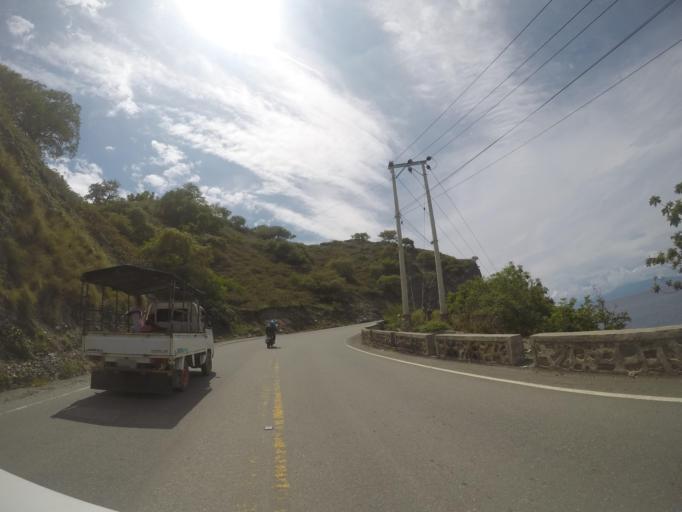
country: TL
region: Liquica
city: Liquica
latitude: -8.5742
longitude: 125.3736
